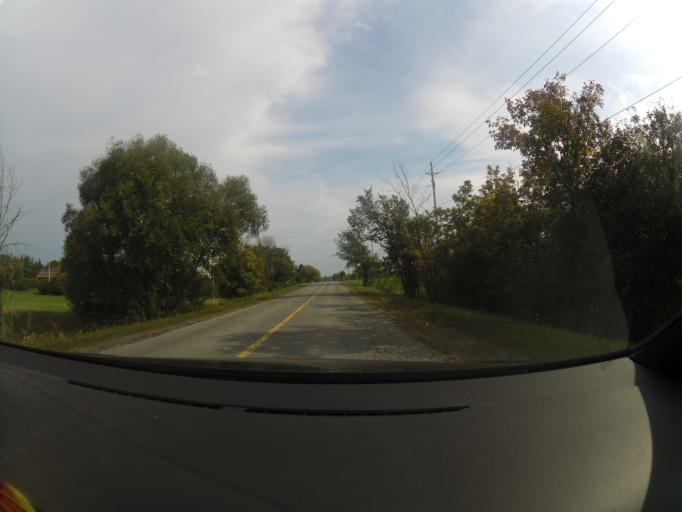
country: CA
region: Ontario
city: Bells Corners
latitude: 45.3917
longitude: -75.9920
